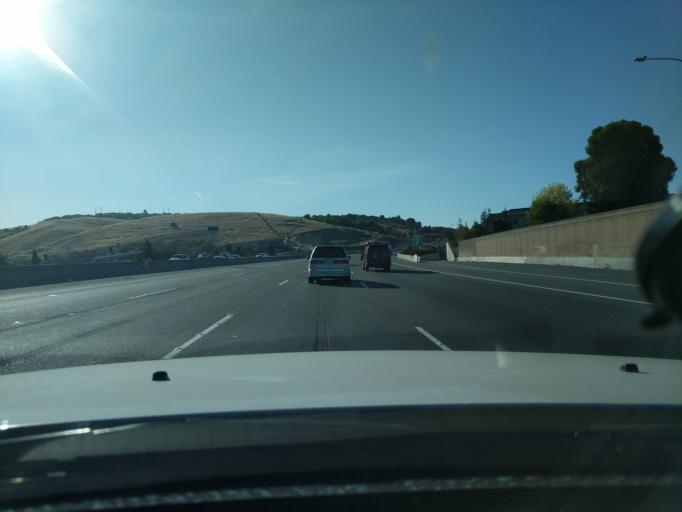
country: US
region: California
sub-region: Santa Clara County
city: Seven Trees
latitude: 37.2977
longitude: -121.8117
